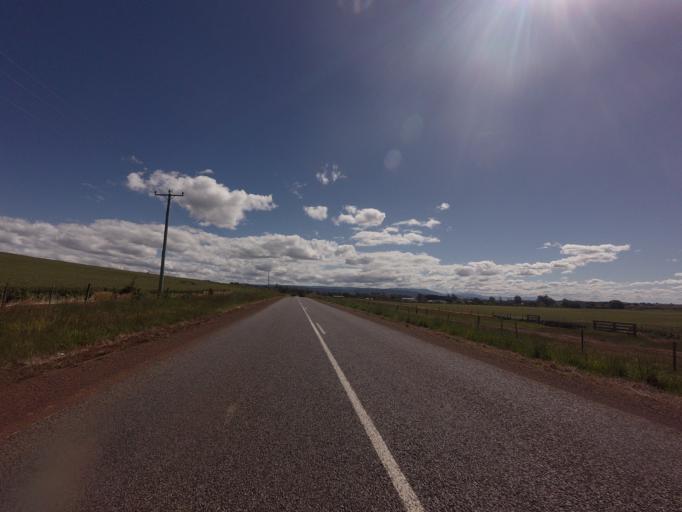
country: AU
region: Tasmania
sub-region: Northern Midlands
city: Evandale
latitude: -41.9402
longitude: 147.5445
